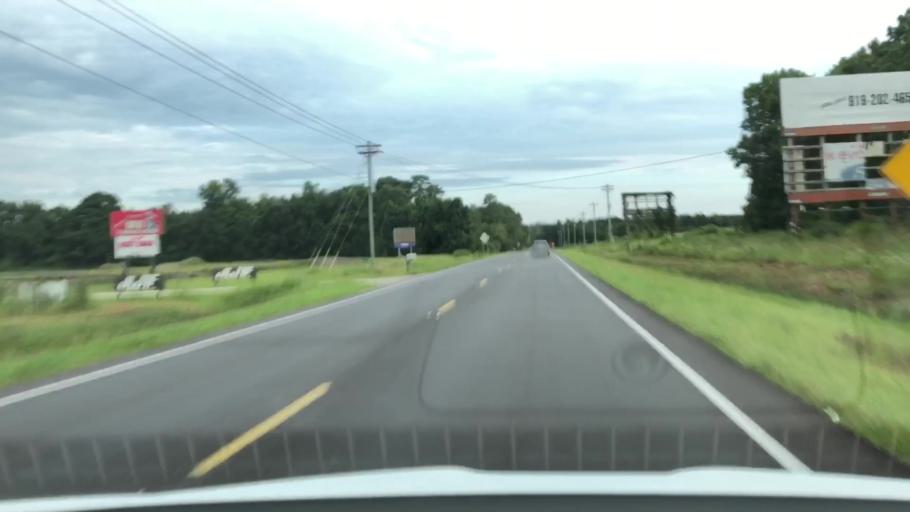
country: US
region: North Carolina
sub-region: Jones County
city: Maysville
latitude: 34.8655
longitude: -77.1919
